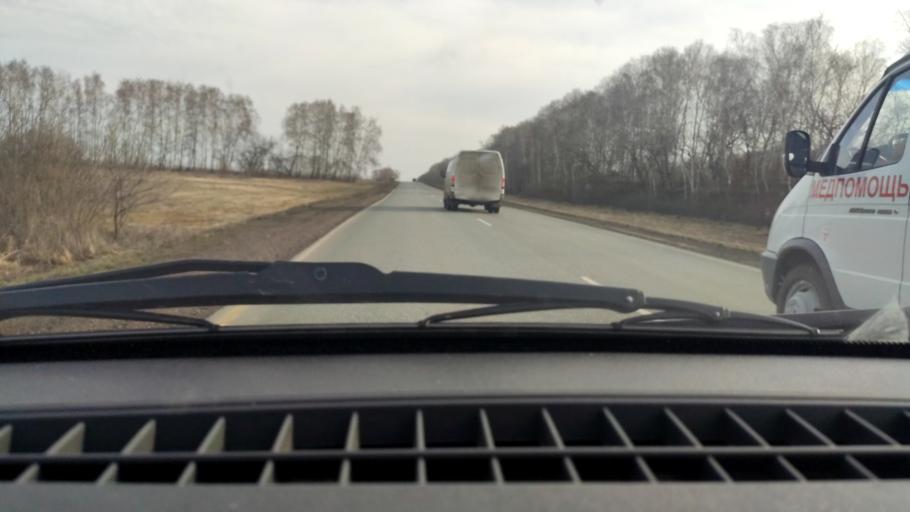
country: RU
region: Bashkortostan
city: Chishmy
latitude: 54.5346
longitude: 55.3110
